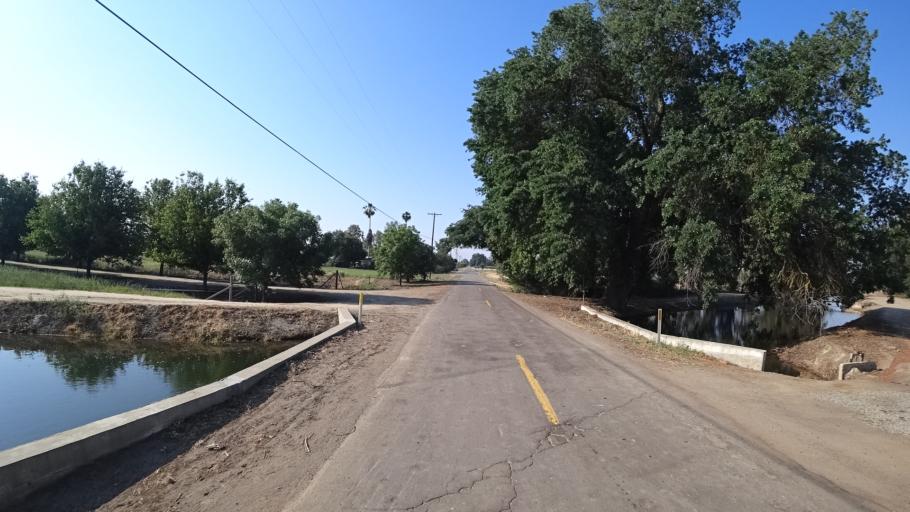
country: US
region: California
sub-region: Fresno County
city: Riverdale
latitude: 36.3698
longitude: -119.8251
